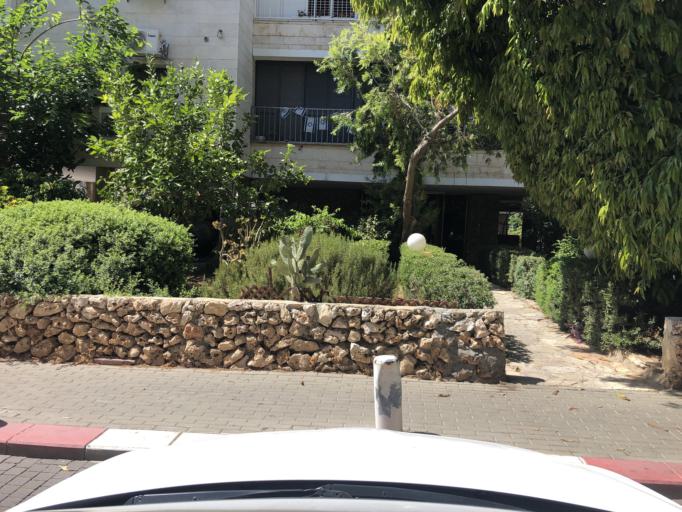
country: IL
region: Tel Aviv
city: Ramat Gan
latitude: 32.0777
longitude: 34.8103
